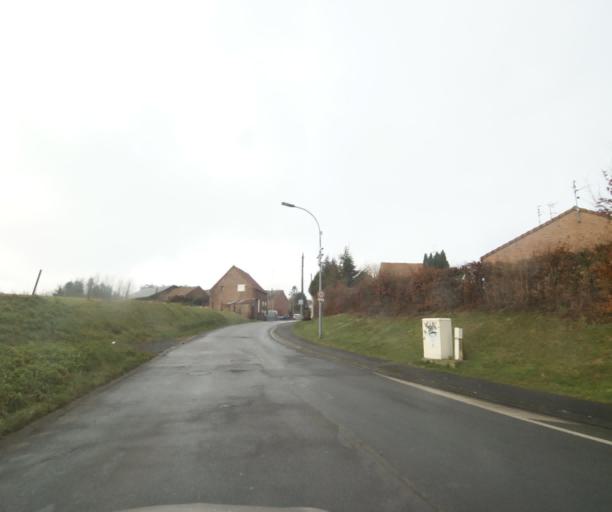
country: FR
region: Nord-Pas-de-Calais
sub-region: Departement du Nord
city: Famars
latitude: 50.3149
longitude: 3.5224
